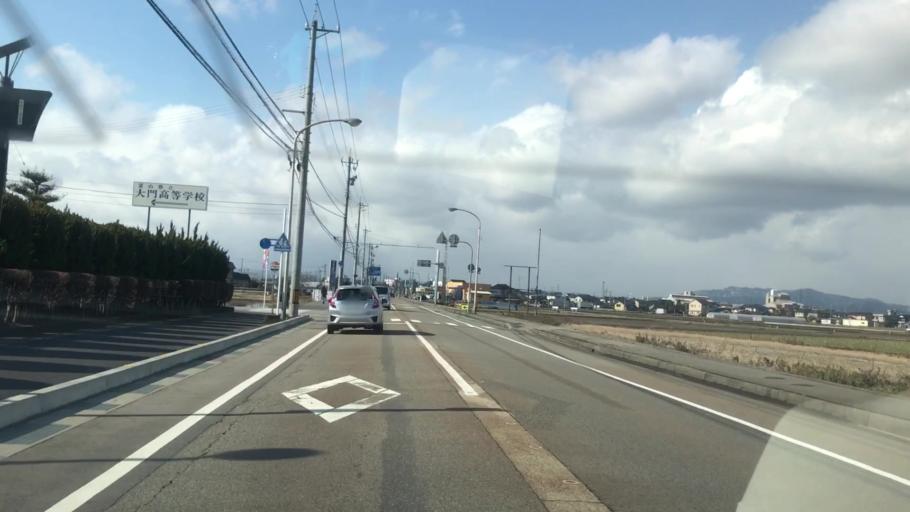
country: JP
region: Toyama
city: Takaoka
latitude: 36.7263
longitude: 137.0634
